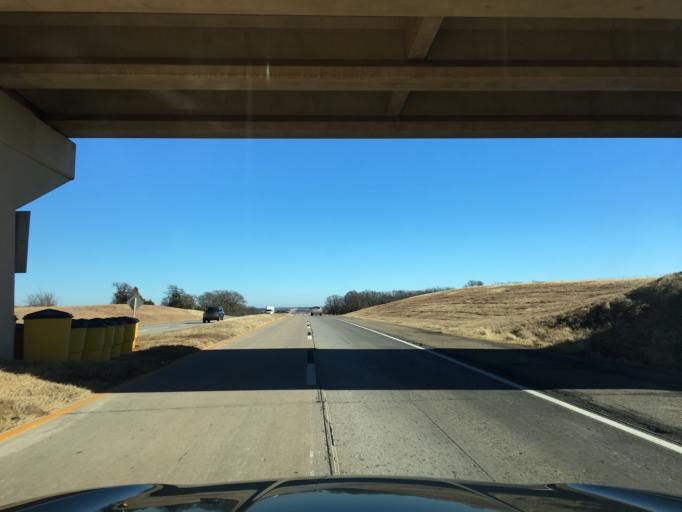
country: US
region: Oklahoma
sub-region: Payne County
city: Yale
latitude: 36.2240
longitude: -96.7487
